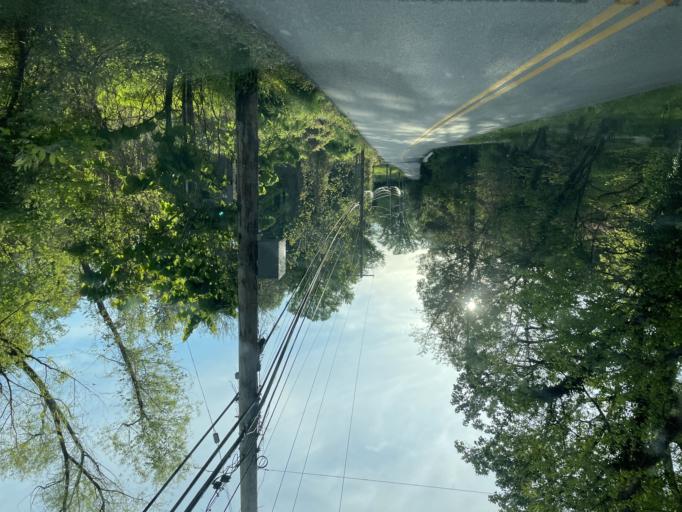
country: US
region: Maryland
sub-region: Baltimore County
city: Lutherville
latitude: 39.4027
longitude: -76.6329
